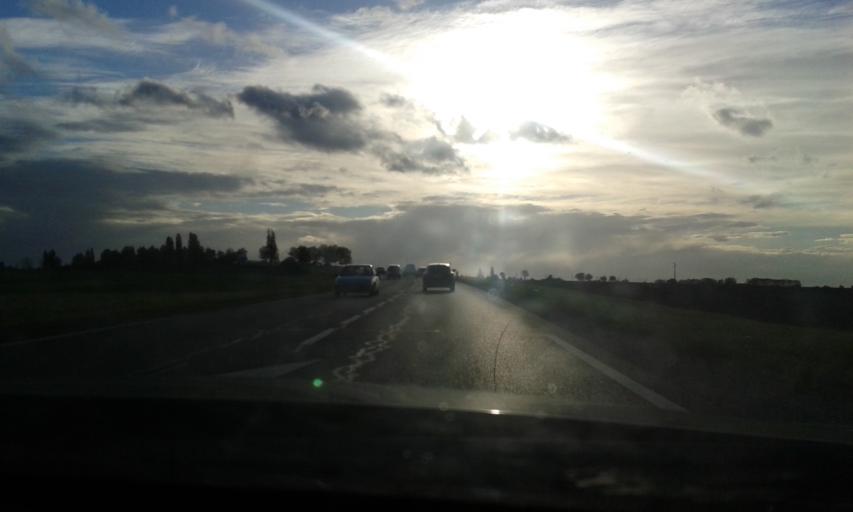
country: FR
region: Centre
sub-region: Departement d'Eure-et-Loir
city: Mainvilliers
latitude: 48.4440
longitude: 1.4341
